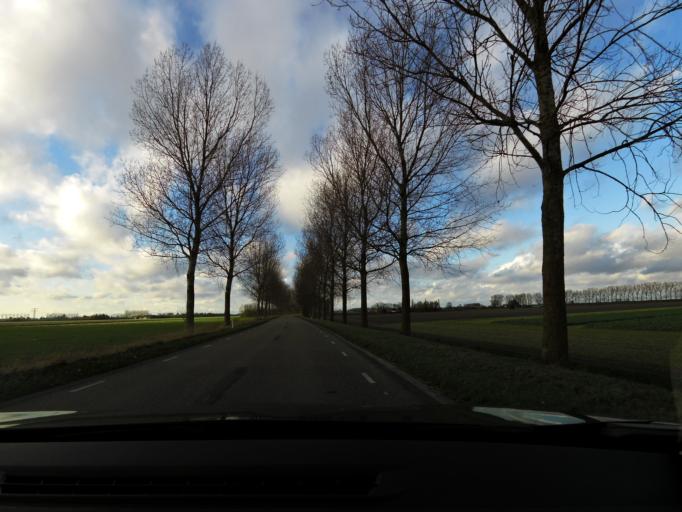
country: NL
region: South Holland
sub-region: Gemeente Goeree-Overflakkee
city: Middelharnis
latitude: 51.7206
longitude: 4.2577
